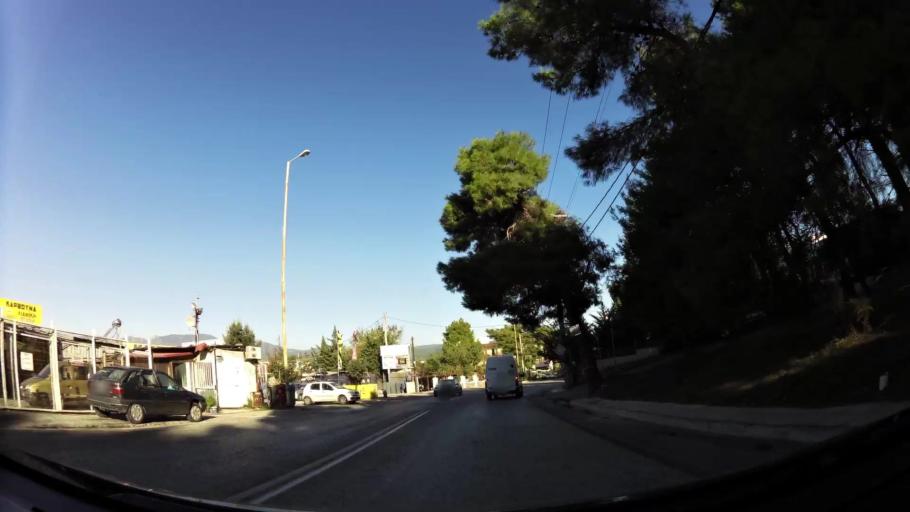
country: GR
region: Attica
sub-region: Nomarchia Anatolikis Attikis
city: Drosia
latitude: 38.1239
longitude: 23.8564
